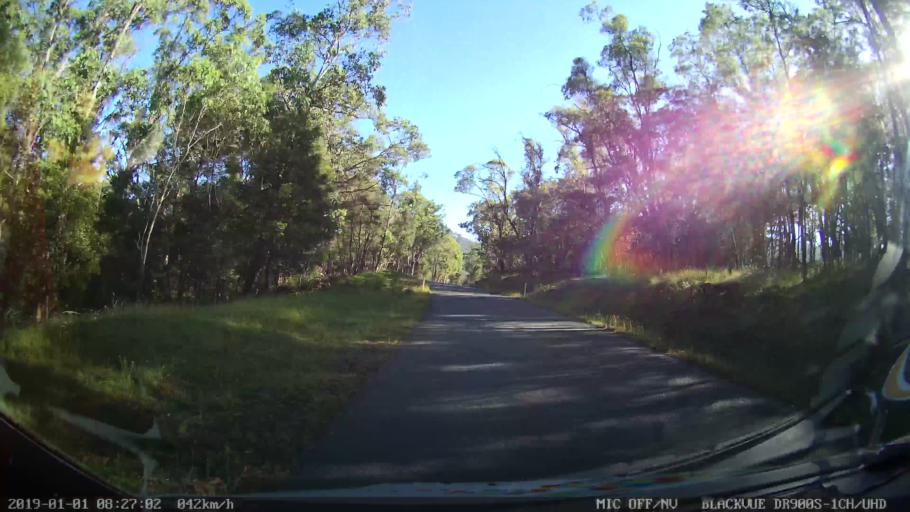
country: AU
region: New South Wales
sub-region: Snowy River
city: Jindabyne
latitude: -36.3844
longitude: 148.1824
